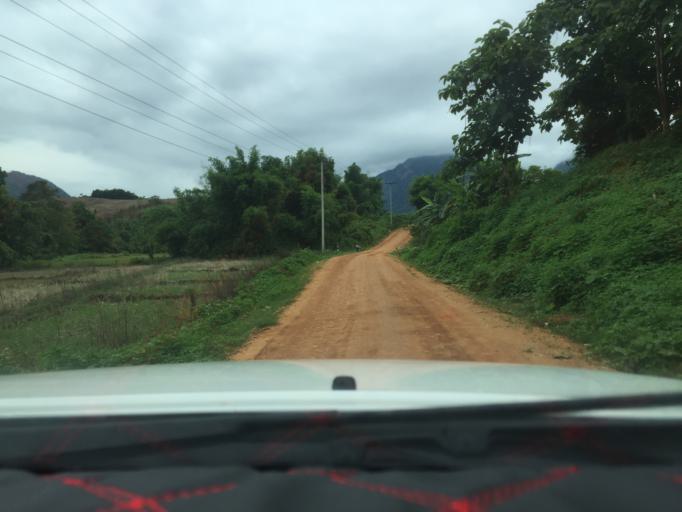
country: TH
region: Phayao
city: Phu Sang
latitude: 19.7716
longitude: 100.5308
